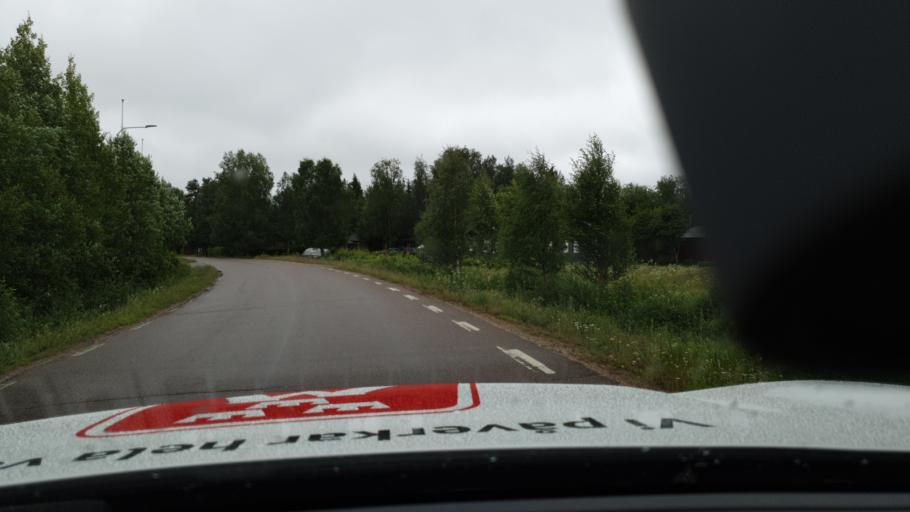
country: SE
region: Norrbotten
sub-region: Overtornea Kommun
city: OEvertornea
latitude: 66.5673
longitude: 23.4222
